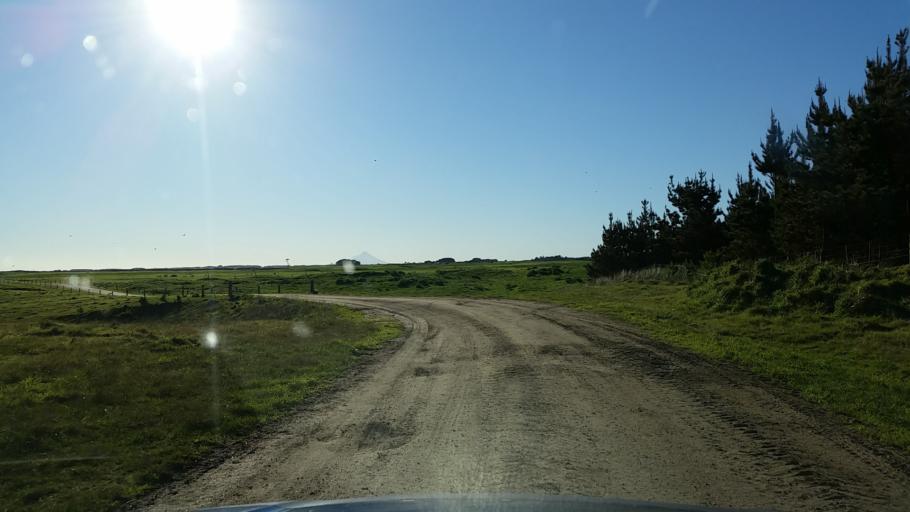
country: NZ
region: Taranaki
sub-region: South Taranaki District
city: Patea
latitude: -39.8318
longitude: 174.6810
